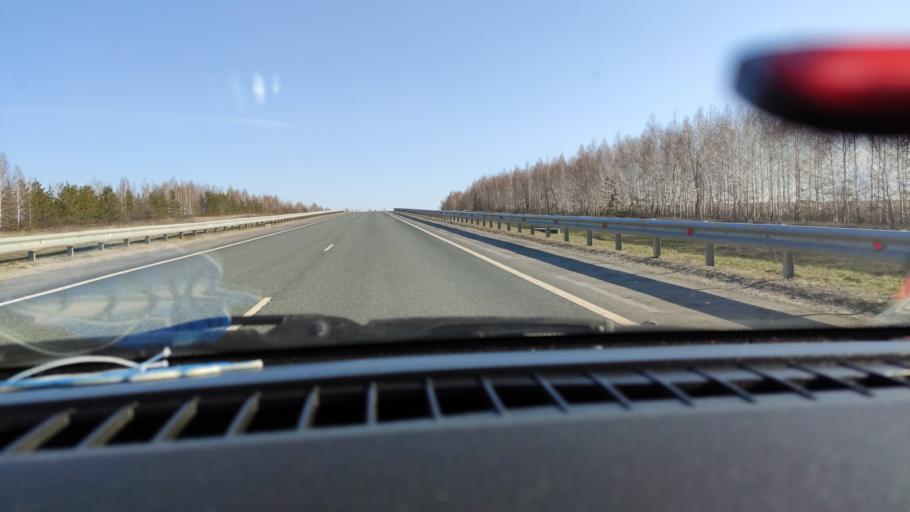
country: RU
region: Saratov
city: Dukhovnitskoye
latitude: 52.8322
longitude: 48.2397
